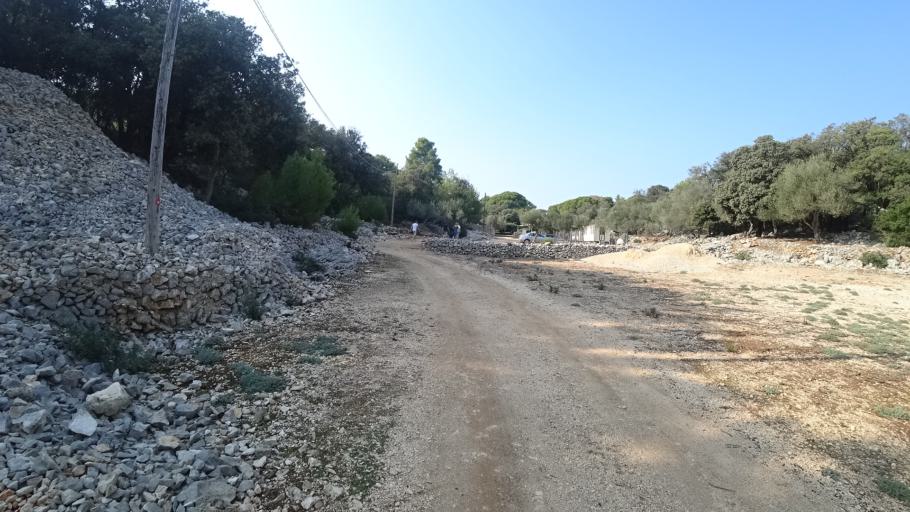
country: HR
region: Primorsko-Goranska
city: Mali Losinj
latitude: 44.4937
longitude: 14.5044
